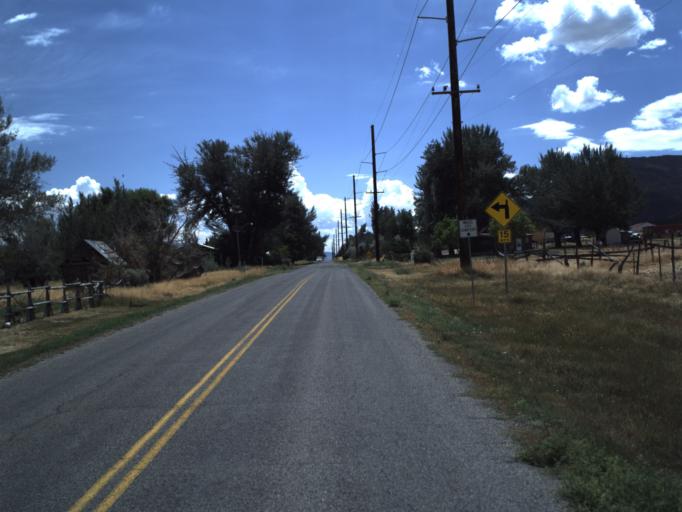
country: US
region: Utah
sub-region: Sanpete County
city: Moroni
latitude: 39.4896
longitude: -111.6389
